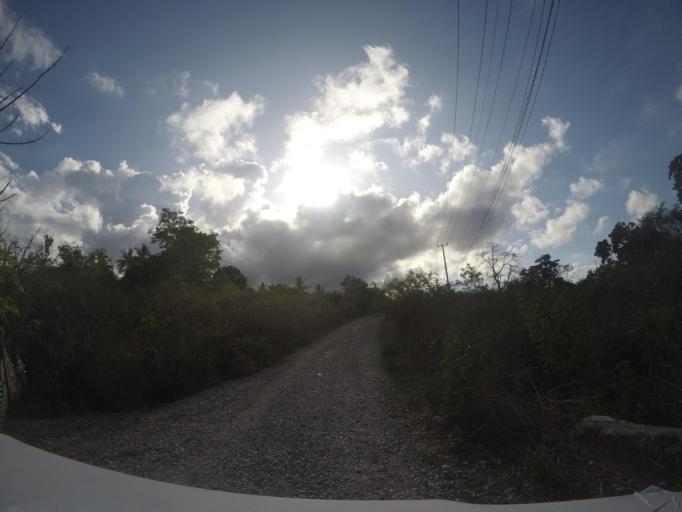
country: TL
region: Baucau
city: Baucau
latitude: -8.4750
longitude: 126.4621
